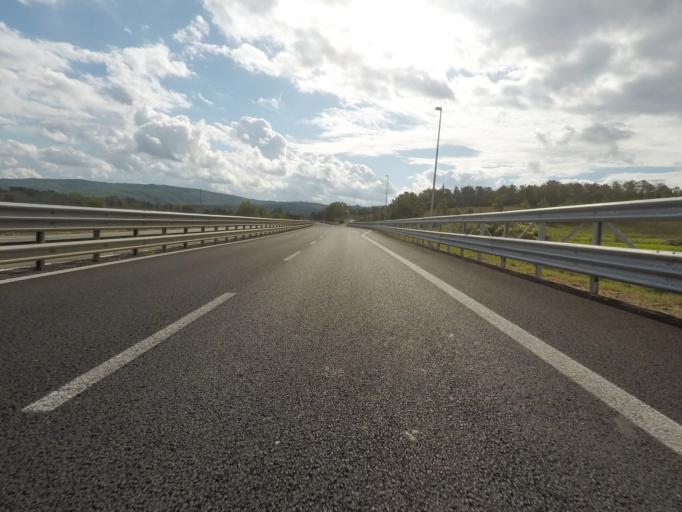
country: IT
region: Tuscany
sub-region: Provincia di Siena
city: Serre di Rapolano
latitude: 43.2569
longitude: 11.6332
